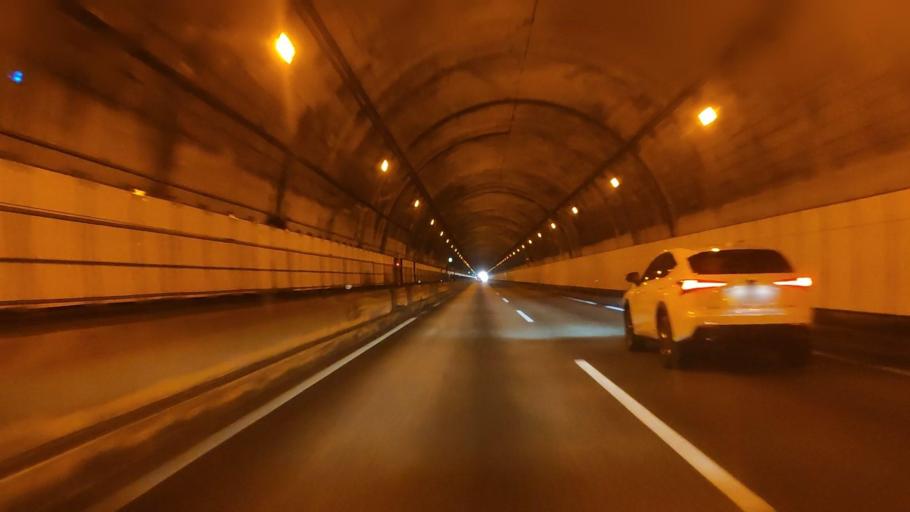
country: JP
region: Miyazaki
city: Miyakonojo
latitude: 31.8232
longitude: 131.2405
